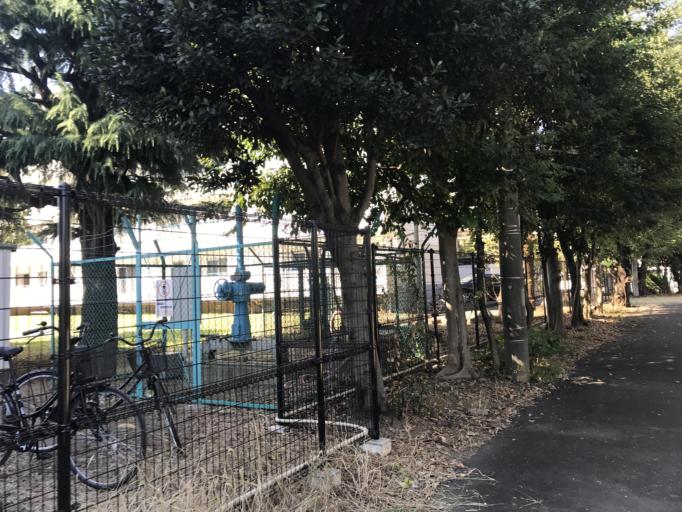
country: JP
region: Tokyo
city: Higashimurayama-shi
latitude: 35.7352
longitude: 139.4720
